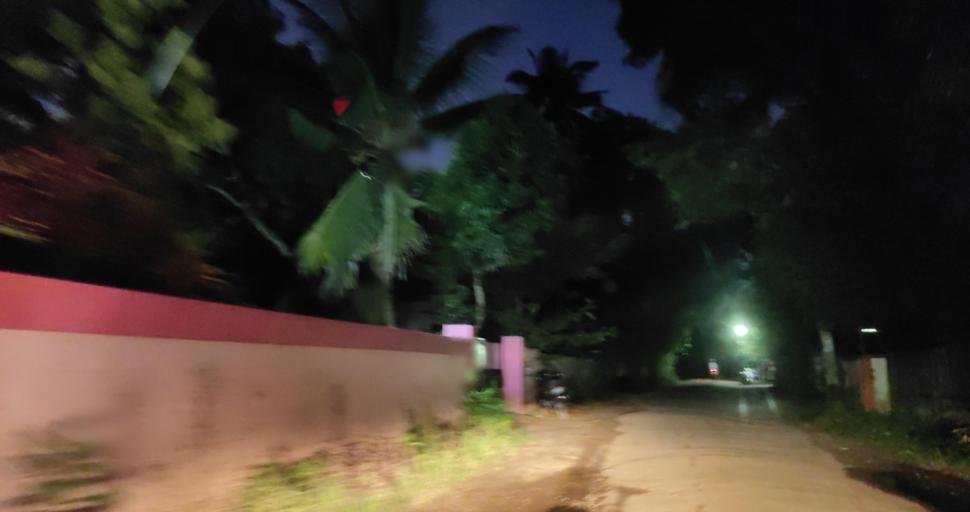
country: IN
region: Kerala
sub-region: Alappuzha
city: Shertallai
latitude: 9.6263
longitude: 76.3382
